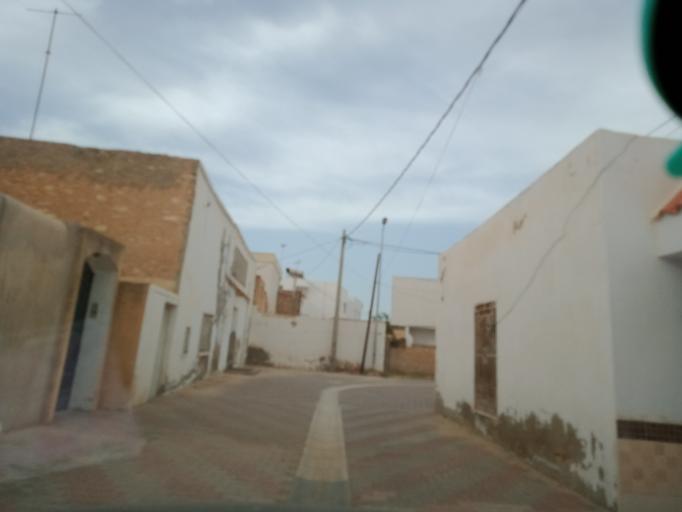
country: TN
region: Safaqis
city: Al Qarmadah
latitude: 34.8021
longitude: 10.7529
